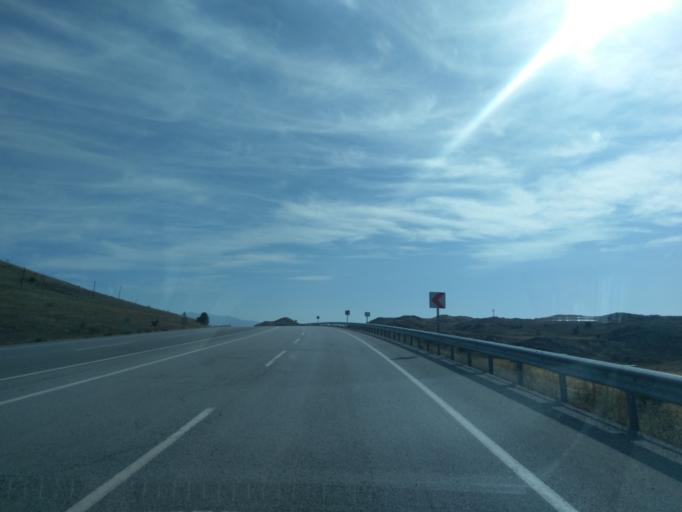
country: TR
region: Sivas
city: Imranli
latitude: 39.8833
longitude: 38.0451
